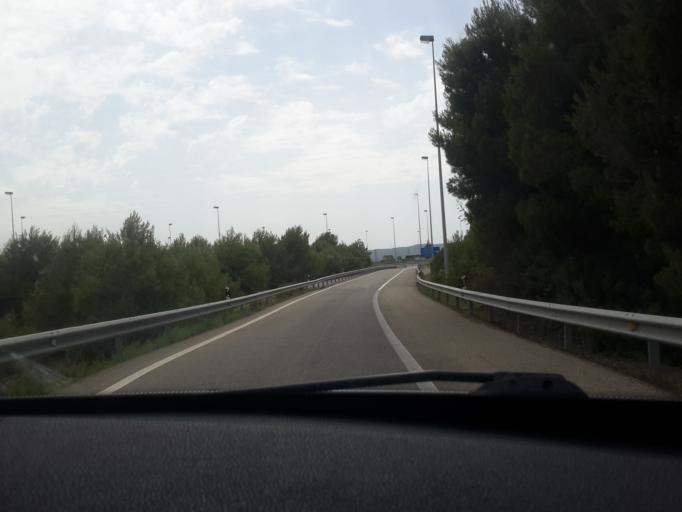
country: ES
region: Catalonia
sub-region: Provincia de Tarragona
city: Santa Oliva
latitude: 41.2686
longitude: 1.5404
